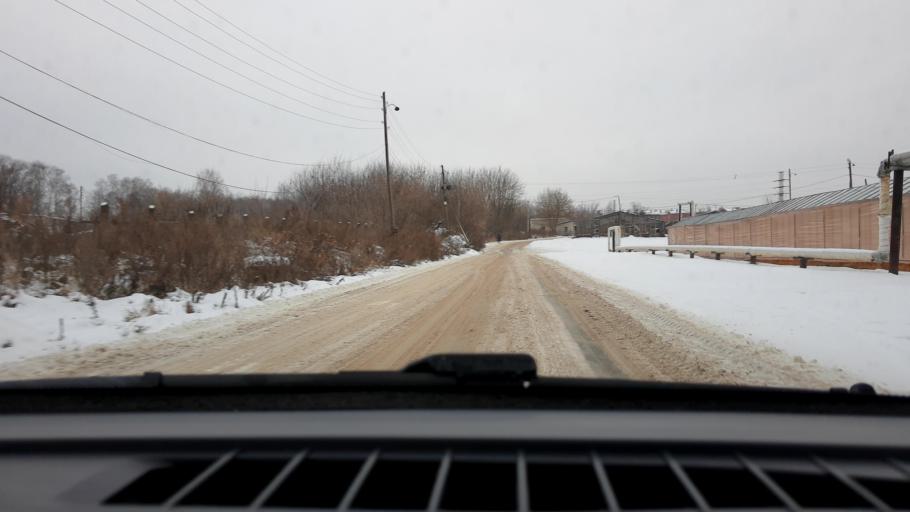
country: RU
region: Nizjnij Novgorod
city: Afonino
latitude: 56.2146
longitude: 44.0967
